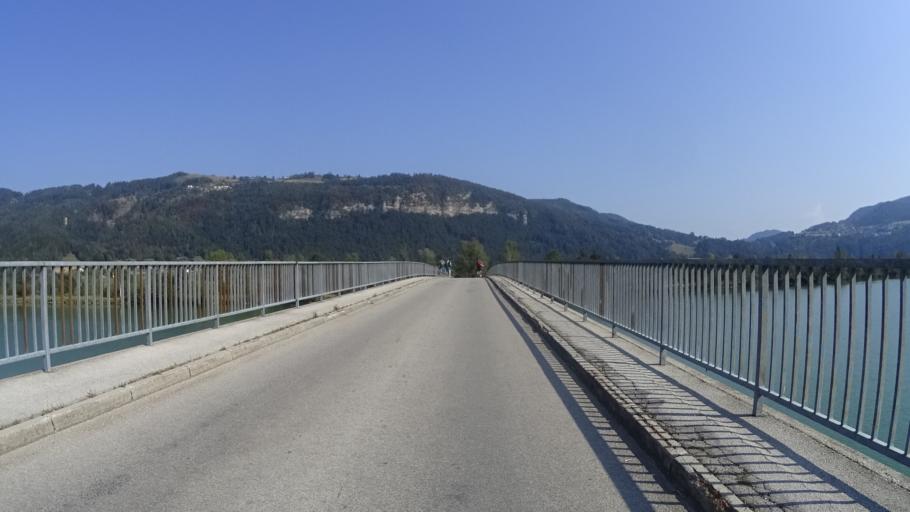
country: AT
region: Carinthia
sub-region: Politischer Bezirk Klagenfurt Land
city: Grafenstein
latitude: 46.5569
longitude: 14.4165
